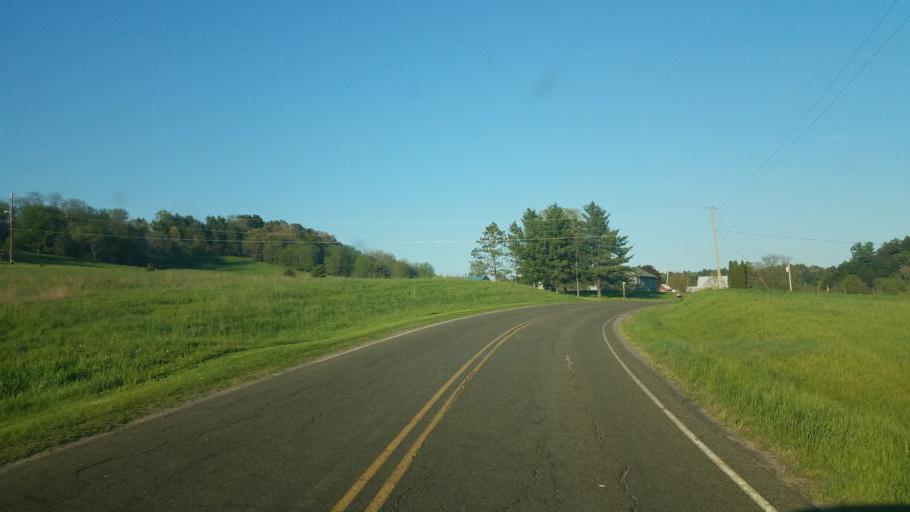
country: US
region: Wisconsin
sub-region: Juneau County
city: Elroy
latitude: 43.6545
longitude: -90.2380
